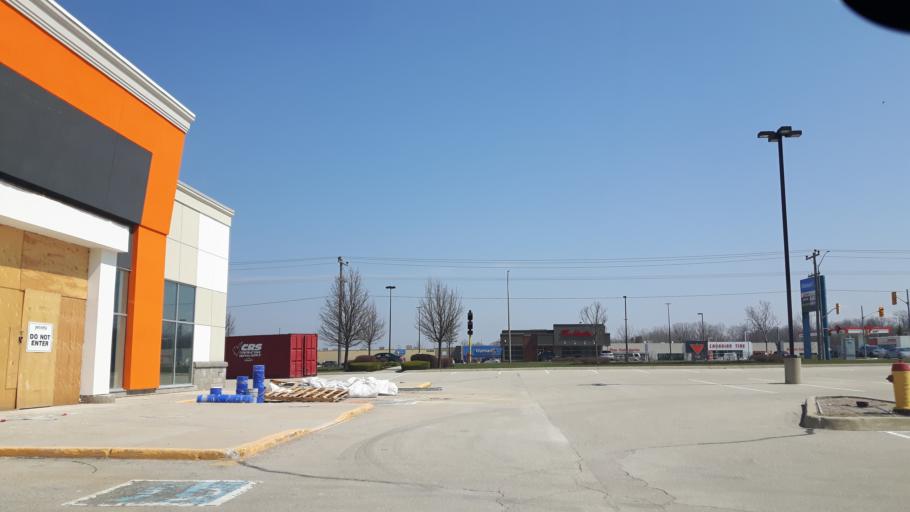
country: CA
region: Ontario
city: Goderich
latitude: 43.7293
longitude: -81.6895
